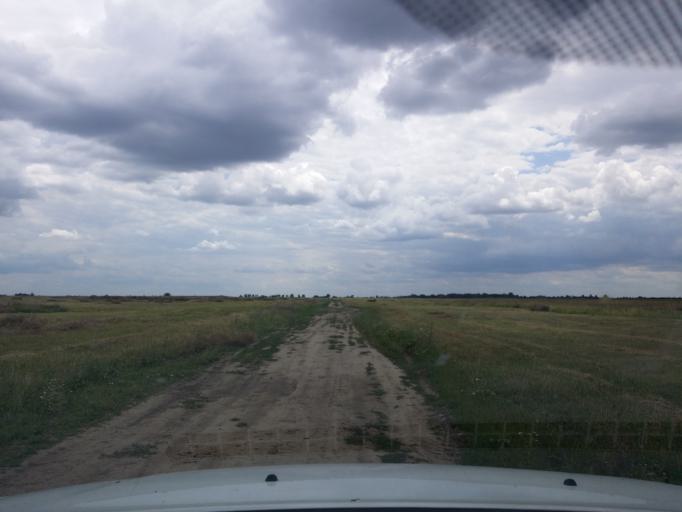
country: HU
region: Hajdu-Bihar
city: Egyek
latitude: 47.5680
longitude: 20.9445
